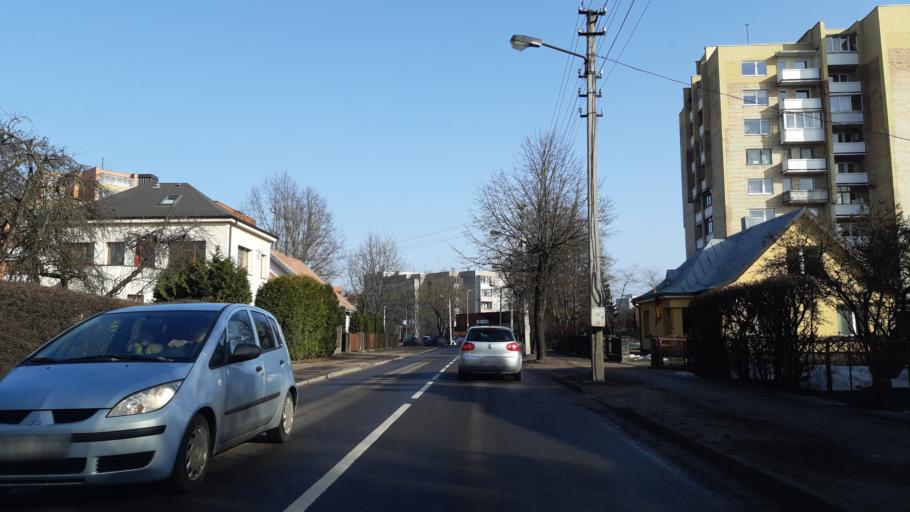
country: LT
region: Kauno apskritis
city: Dainava (Kaunas)
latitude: 54.9088
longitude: 23.9547
